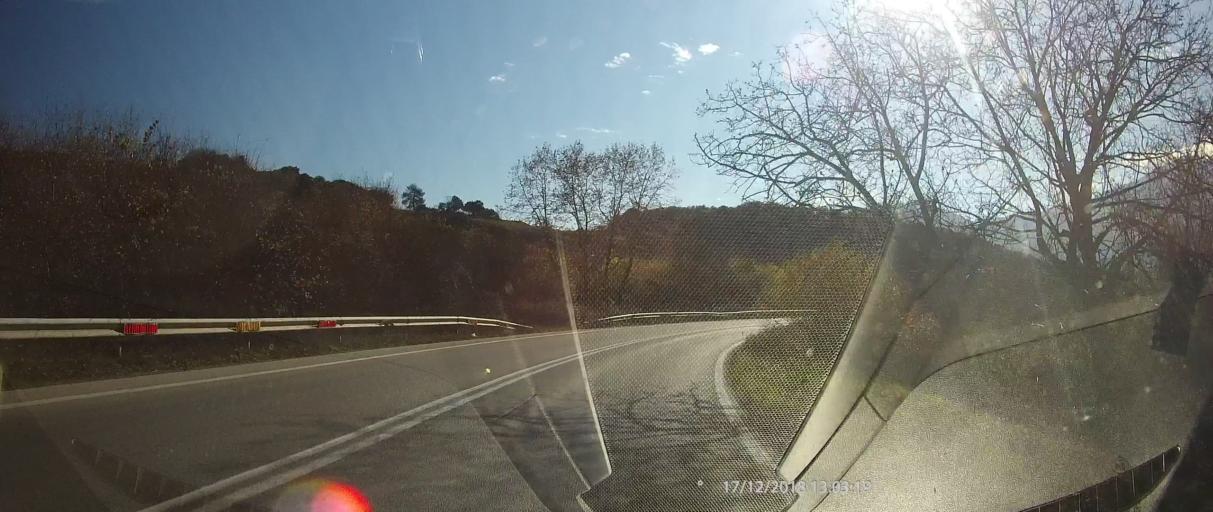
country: GR
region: Thessaly
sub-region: Trikala
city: Kastraki
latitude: 39.7139
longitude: 21.6022
